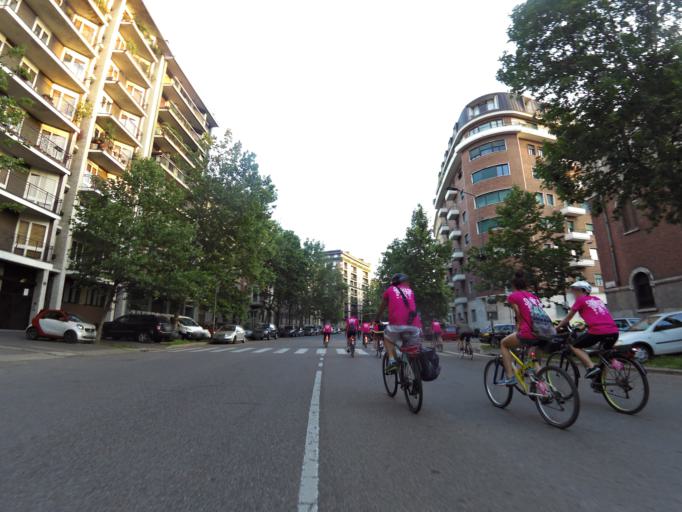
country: IT
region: Lombardy
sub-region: Citta metropolitana di Milano
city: Milano
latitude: 45.4748
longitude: 9.1690
